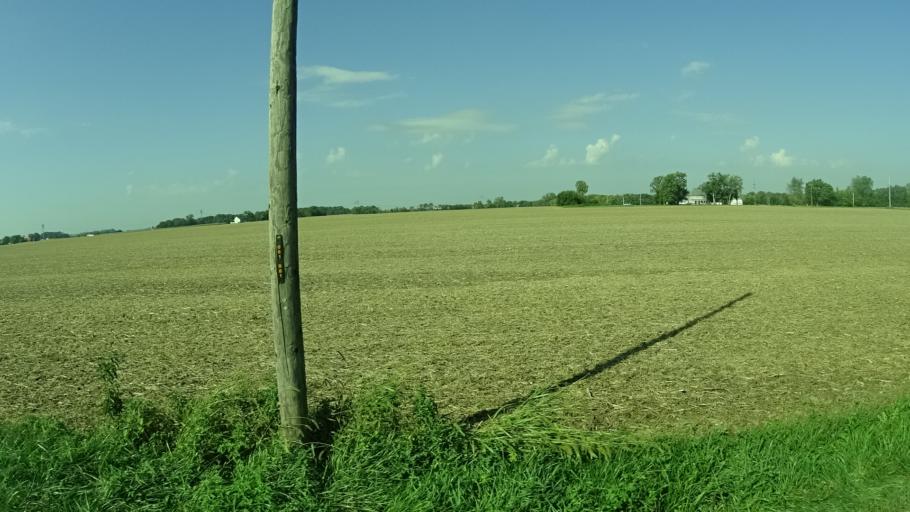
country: US
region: Indiana
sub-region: Madison County
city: Lapel
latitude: 40.0582
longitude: -85.8534
